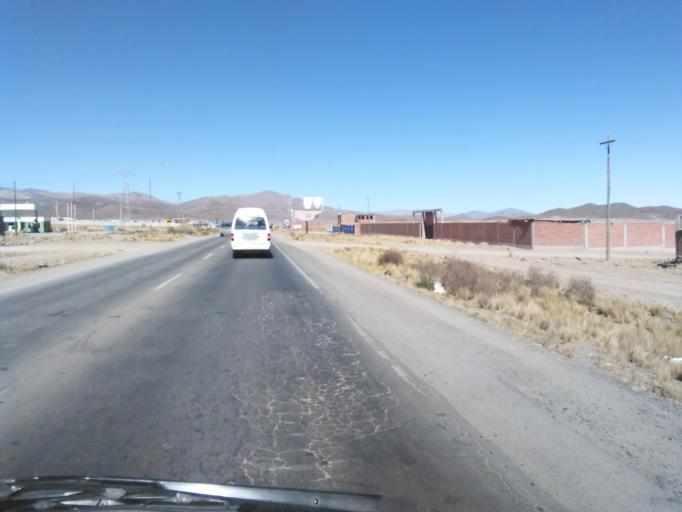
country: BO
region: Oruro
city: Oruro
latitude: -18.0152
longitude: -67.0336
